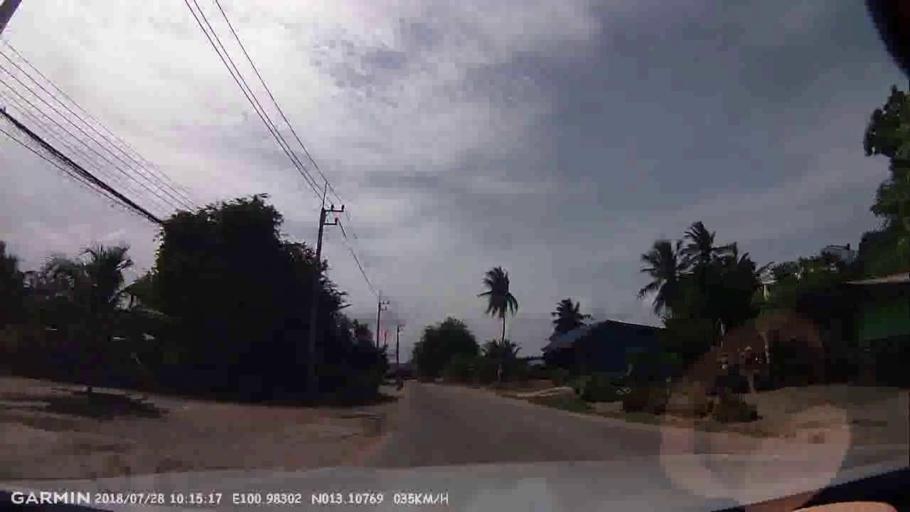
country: TH
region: Chon Buri
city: Ban Talat Bueng
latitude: 13.1077
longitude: 100.9832
